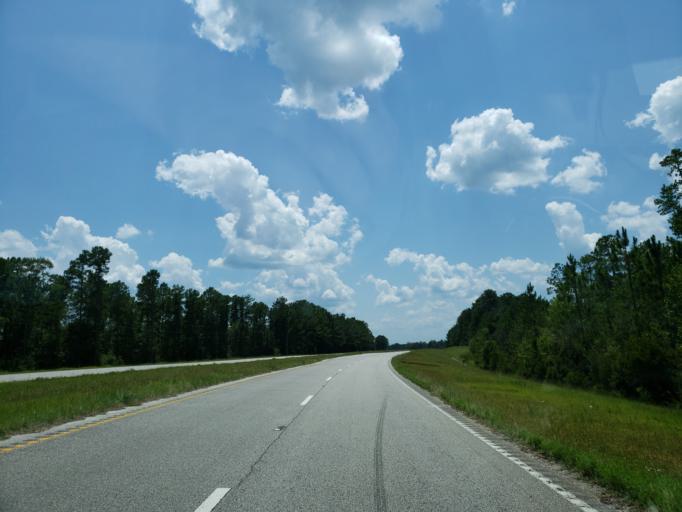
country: US
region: Mississippi
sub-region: Wayne County
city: Belmont
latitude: 31.3685
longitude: -88.4883
